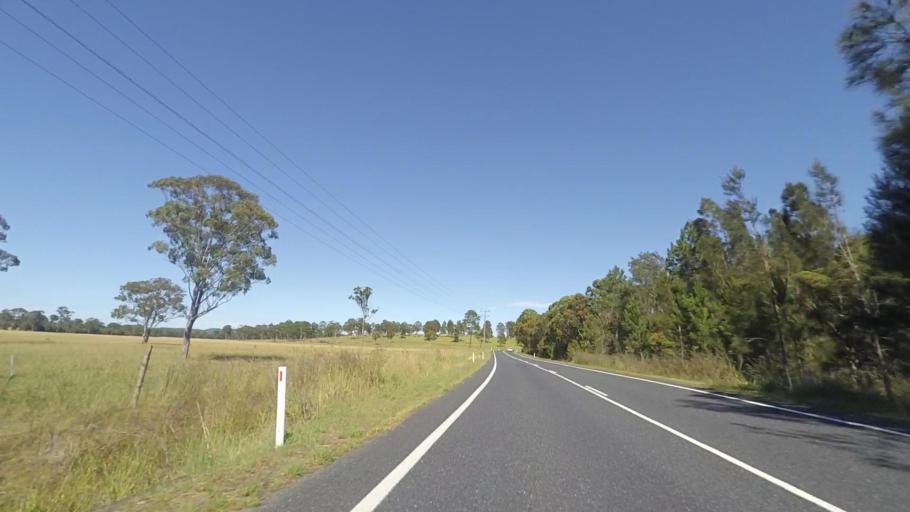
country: AU
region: New South Wales
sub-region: Great Lakes
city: Hawks Nest
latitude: -32.6142
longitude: 152.0994
